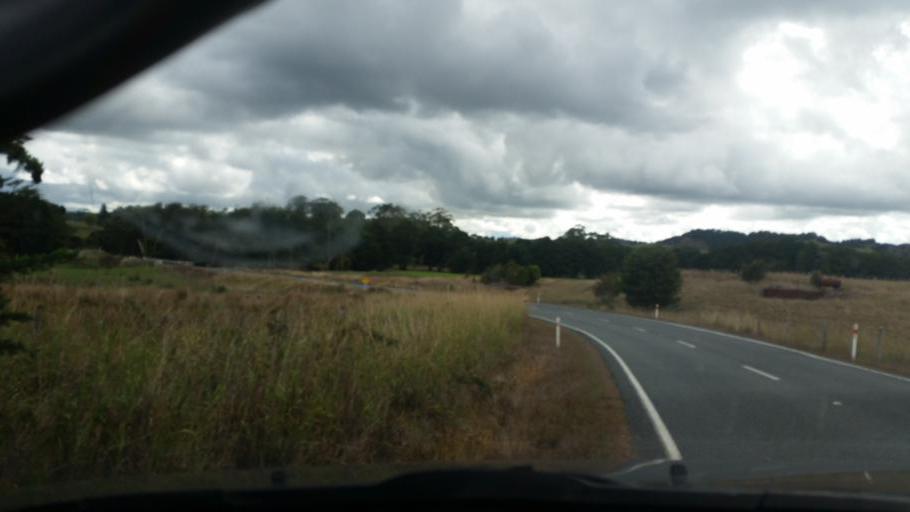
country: NZ
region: Northland
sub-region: Whangarei
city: Ruakaka
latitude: -35.9972
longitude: 174.2937
